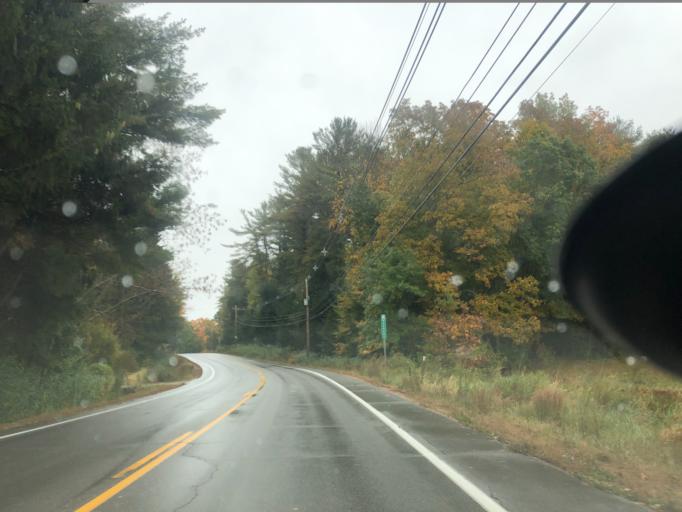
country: US
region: New Hampshire
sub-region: Strafford County
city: Madbury
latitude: 43.1610
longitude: -70.9549
